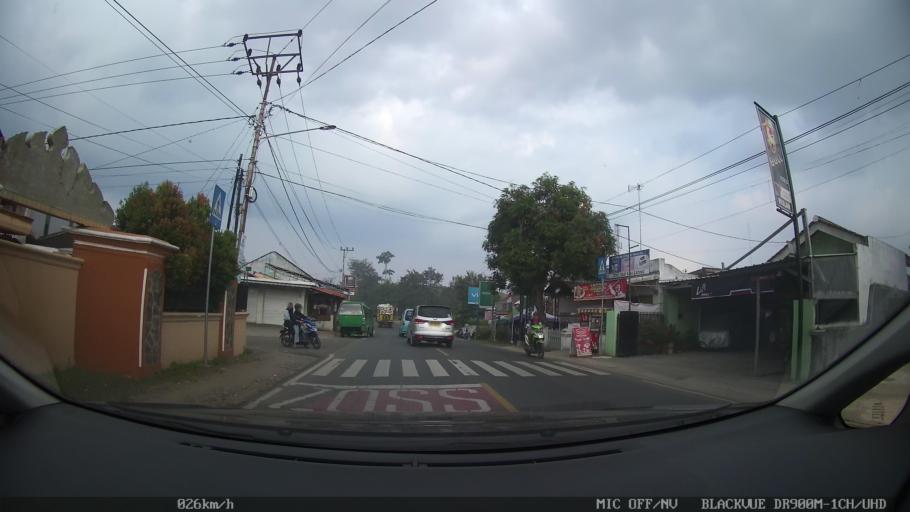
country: ID
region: Lampung
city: Gadingrejo
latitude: -5.3747
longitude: 105.0630
